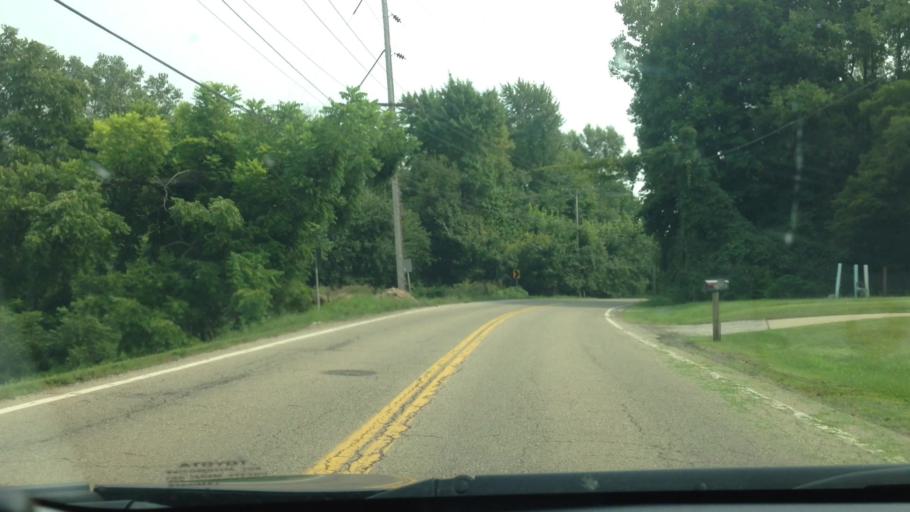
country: US
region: Ohio
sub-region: Summit County
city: Fairlawn
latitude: 41.0875
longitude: -81.5909
